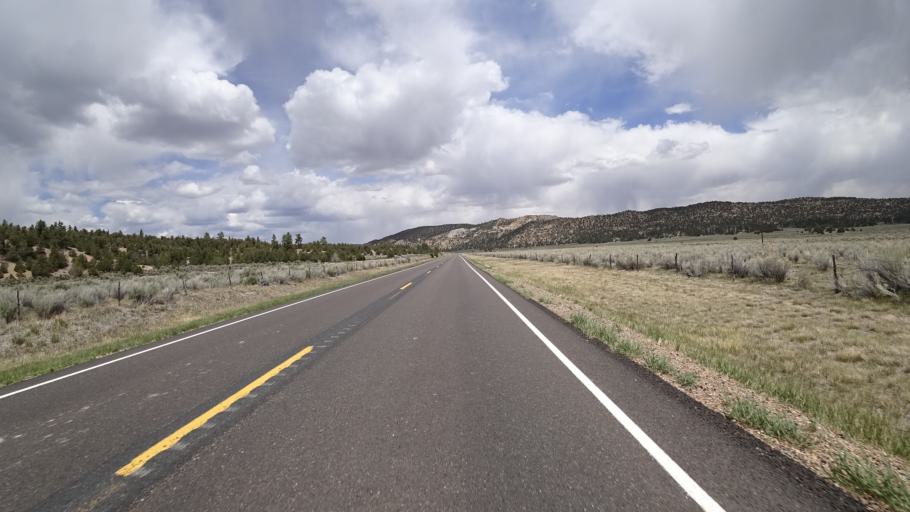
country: US
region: Utah
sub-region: Garfield County
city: Panguitch
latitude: 37.6920
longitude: -111.7995
